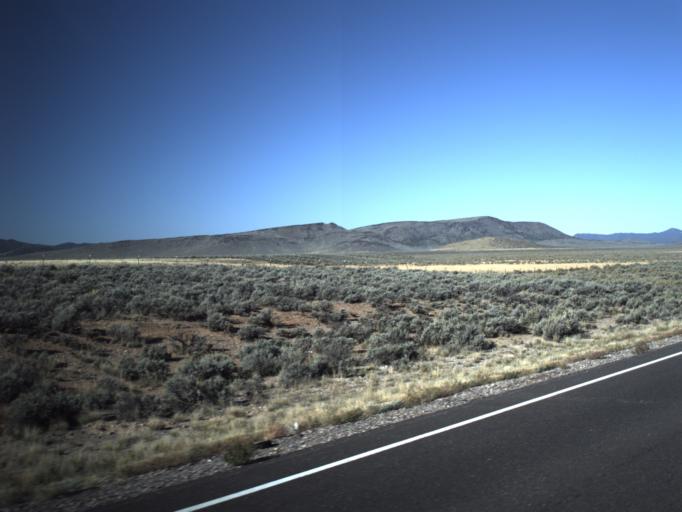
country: US
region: Utah
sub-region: Washington County
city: Enterprise
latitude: 37.7699
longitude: -113.8275
